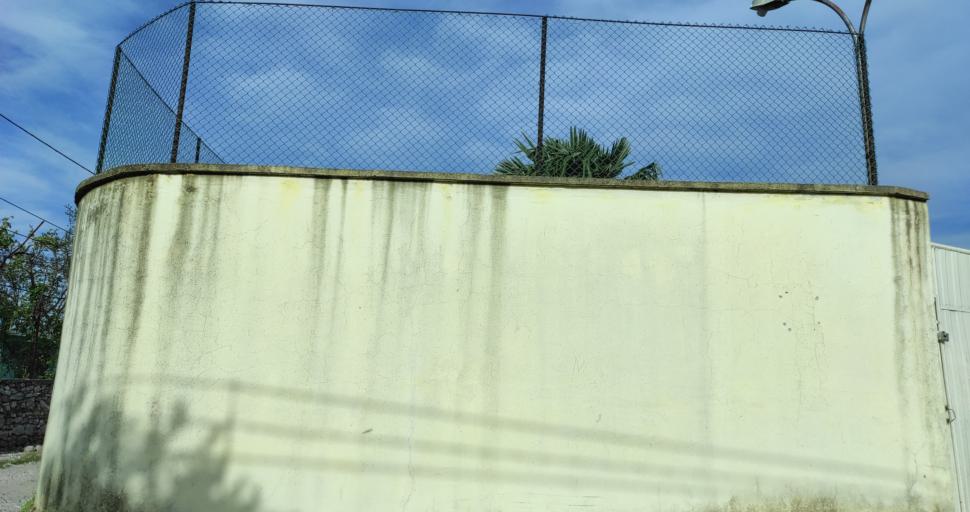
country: AL
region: Shkoder
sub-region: Rrethi i Shkodres
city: Shkoder
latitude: 42.0580
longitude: 19.5277
